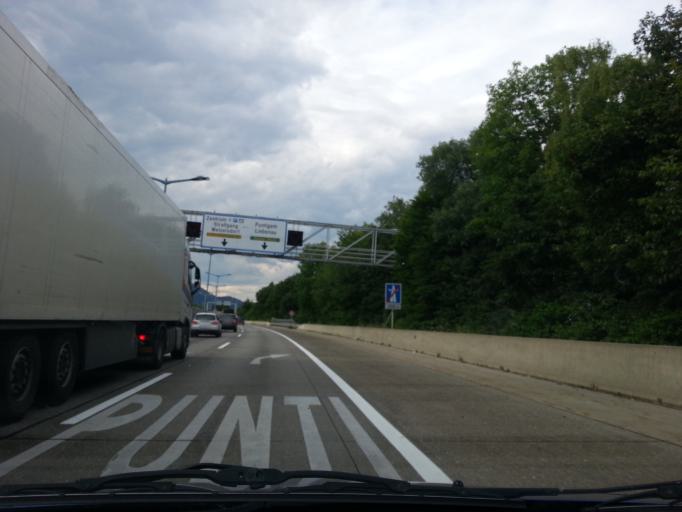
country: AT
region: Styria
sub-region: Graz Stadt
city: Wetzelsdorf
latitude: 47.0305
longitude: 15.4132
